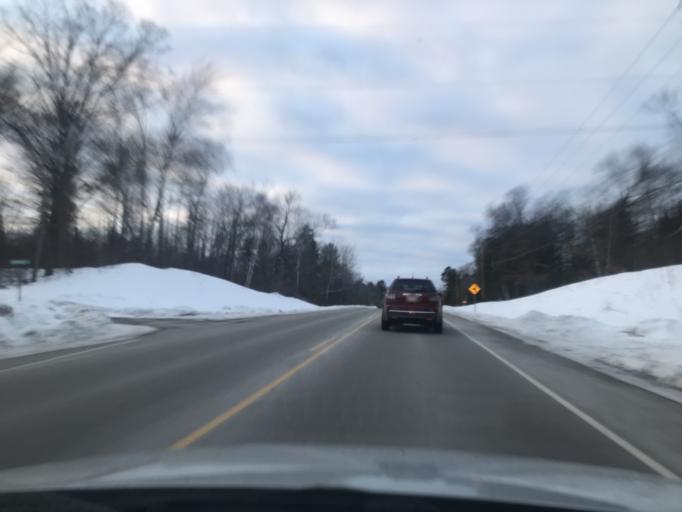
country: US
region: Wisconsin
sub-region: Marinette County
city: Marinette
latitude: 45.1582
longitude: -87.7173
